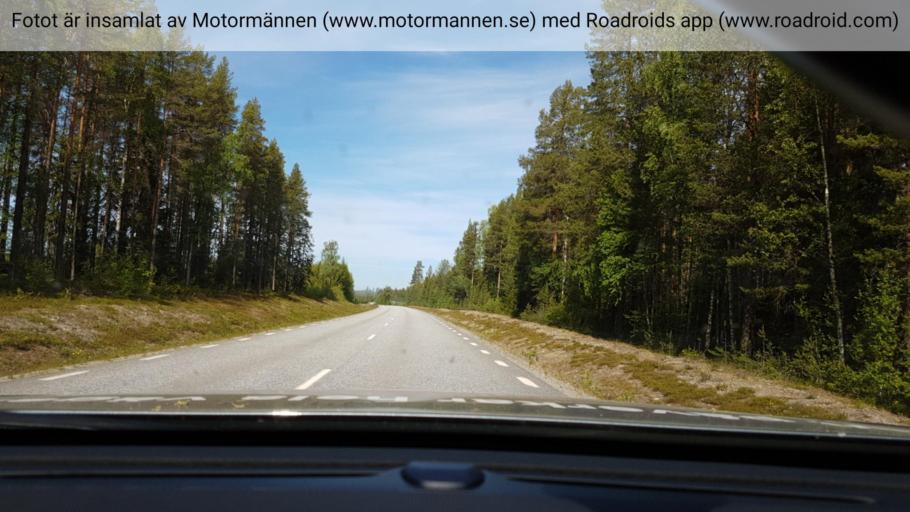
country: SE
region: Vaesterbotten
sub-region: Asele Kommun
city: Asele
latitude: 64.2190
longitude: 16.8908
